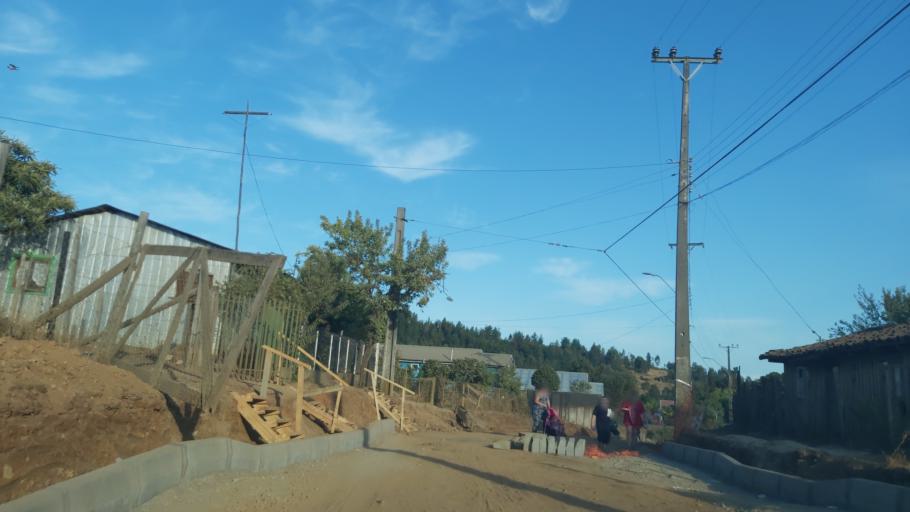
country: CL
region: Biobio
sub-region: Provincia de Biobio
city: La Laja
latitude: -37.1604
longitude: -72.9099
